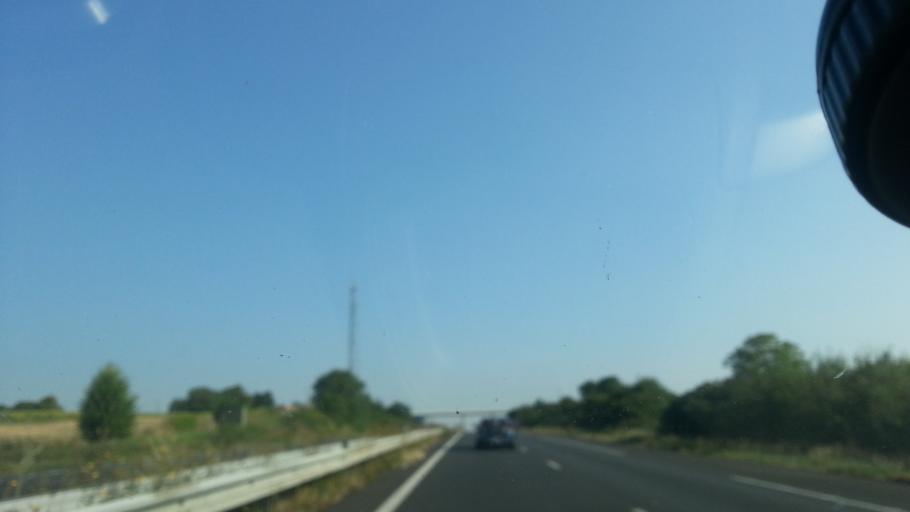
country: FR
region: Poitou-Charentes
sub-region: Departement de la Vienne
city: Les Ormes
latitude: 46.9816
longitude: 0.5472
